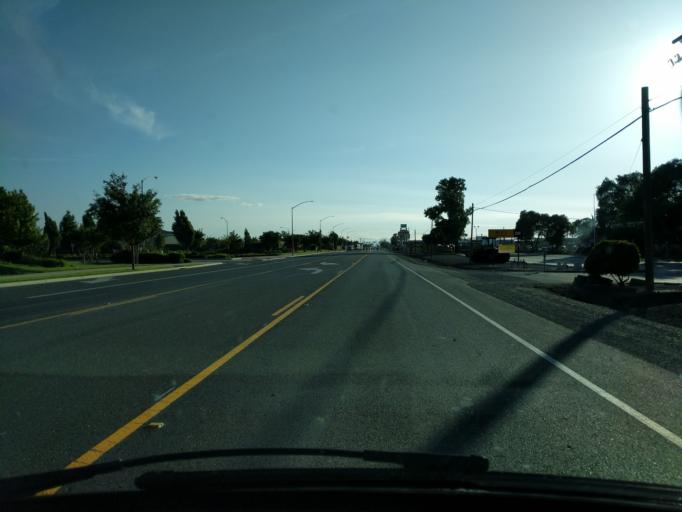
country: US
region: California
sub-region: San Joaquin County
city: Stockton
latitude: 37.9344
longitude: -121.3068
